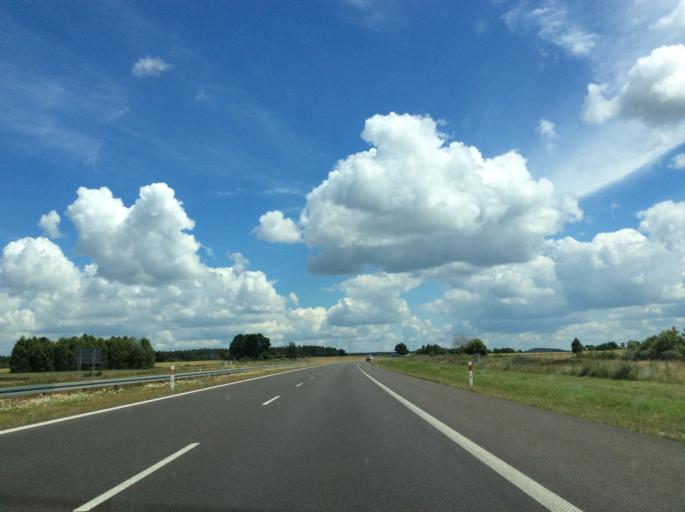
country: PL
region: Greater Poland Voivodeship
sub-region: Powiat turecki
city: Wladyslawow
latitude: 52.1526
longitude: 18.4709
